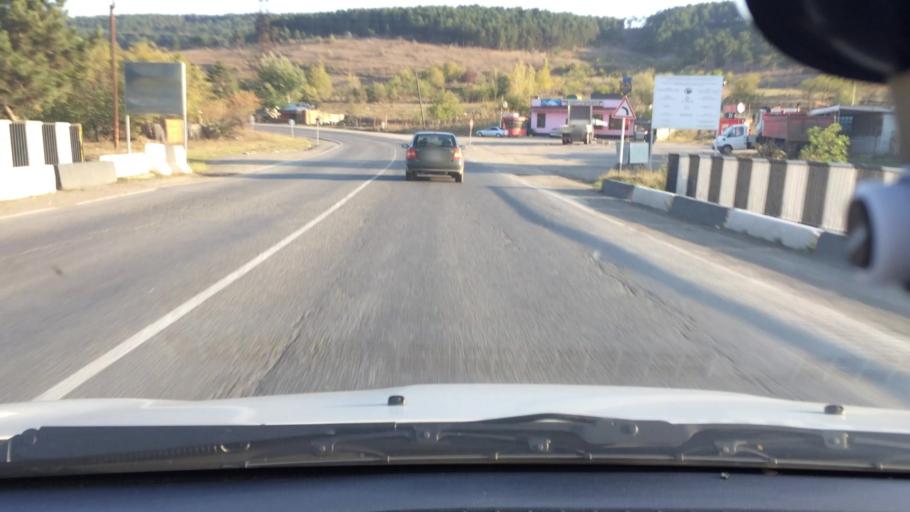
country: GE
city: Surami
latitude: 42.0103
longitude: 43.5778
